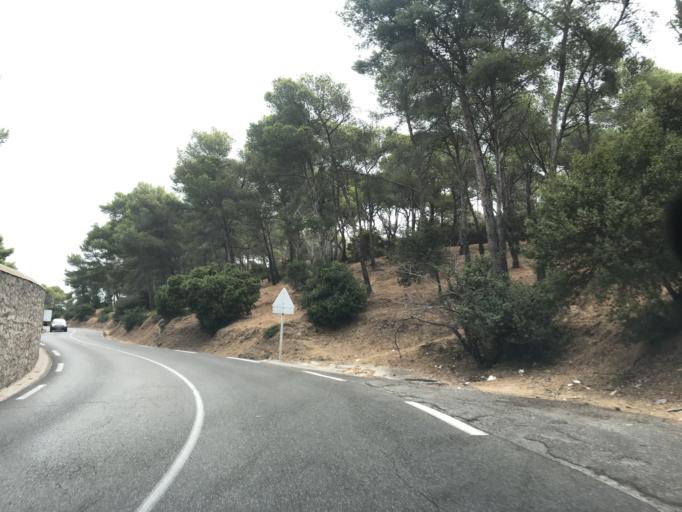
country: FR
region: Provence-Alpes-Cote d'Azur
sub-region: Departement du Var
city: Saint-Mandrier-sur-Mer
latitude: 43.0801
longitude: 5.9120
